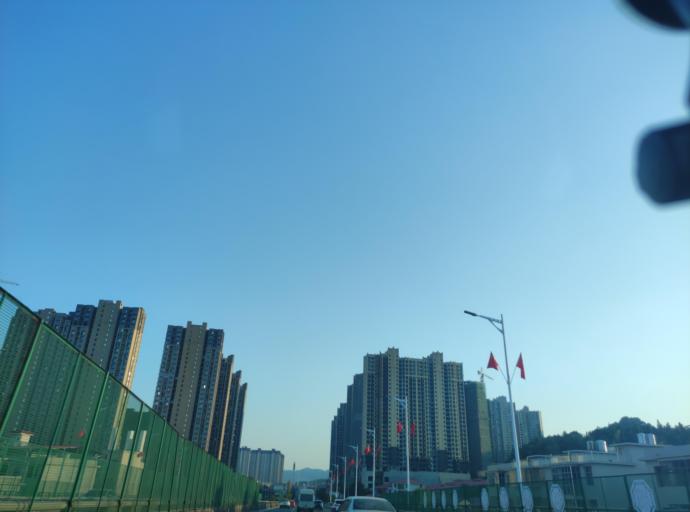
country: CN
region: Jiangxi Sheng
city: Pingxiang
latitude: 27.6384
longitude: 113.8296
